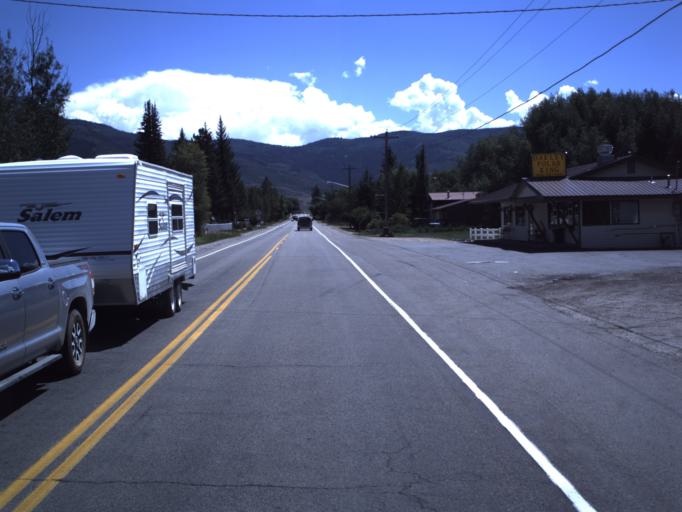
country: US
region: Utah
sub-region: Summit County
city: Oakley
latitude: 40.7124
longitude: -111.2996
